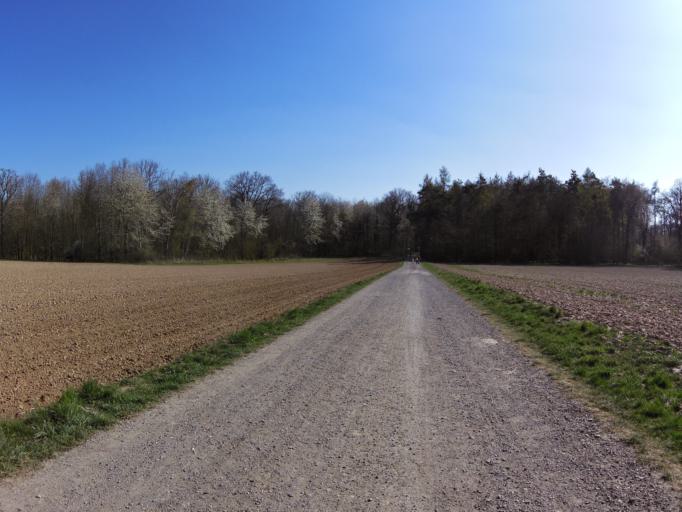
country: DE
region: Bavaria
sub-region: Regierungsbezirk Unterfranken
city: Kurnach
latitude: 49.8349
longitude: 10.0627
